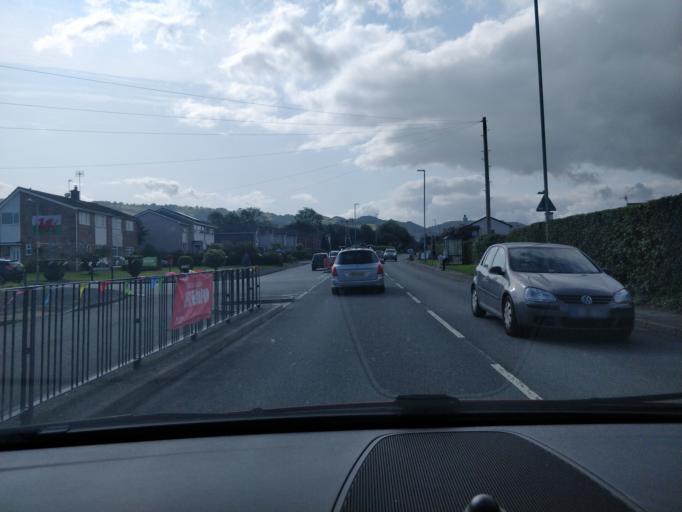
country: GB
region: Wales
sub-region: Conwy
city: Llanrwst
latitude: 53.1333
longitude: -3.7910
